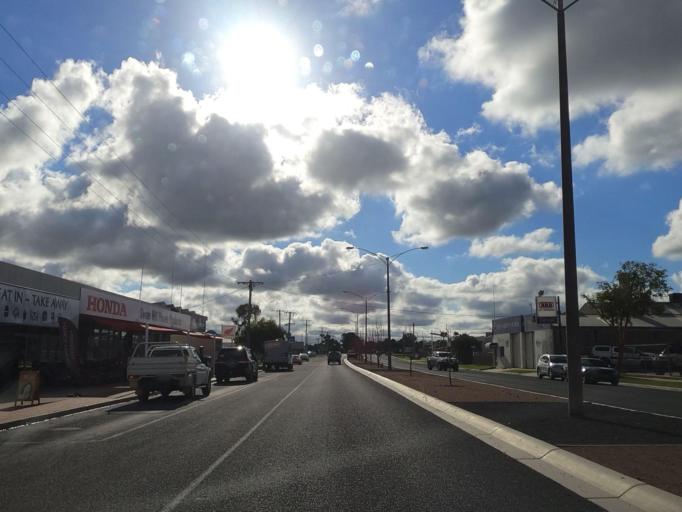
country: AU
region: Victoria
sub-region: Swan Hill
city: Swan Hill
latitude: -35.3303
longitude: 143.5546
